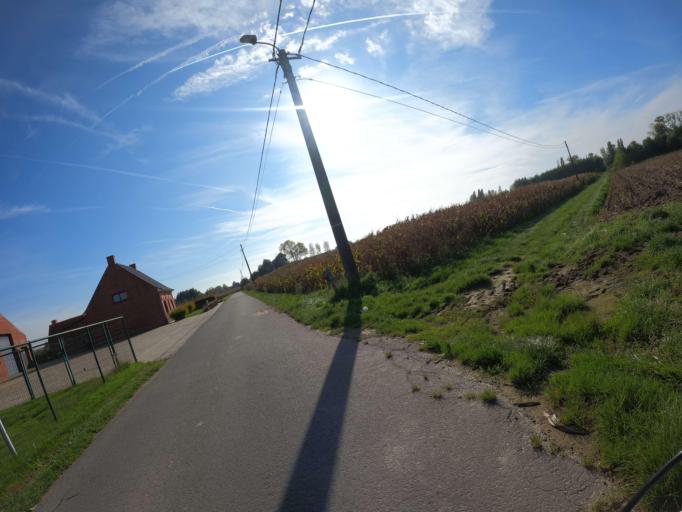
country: BE
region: Flanders
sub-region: Provincie West-Vlaanderen
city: Ruiselede
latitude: 51.0372
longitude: 3.3859
